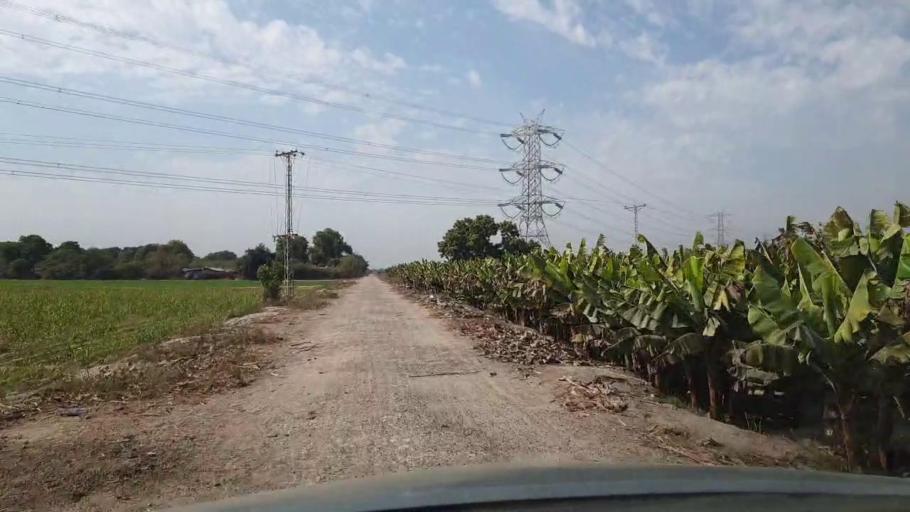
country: PK
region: Sindh
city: Tando Jam
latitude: 25.5617
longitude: 68.5992
